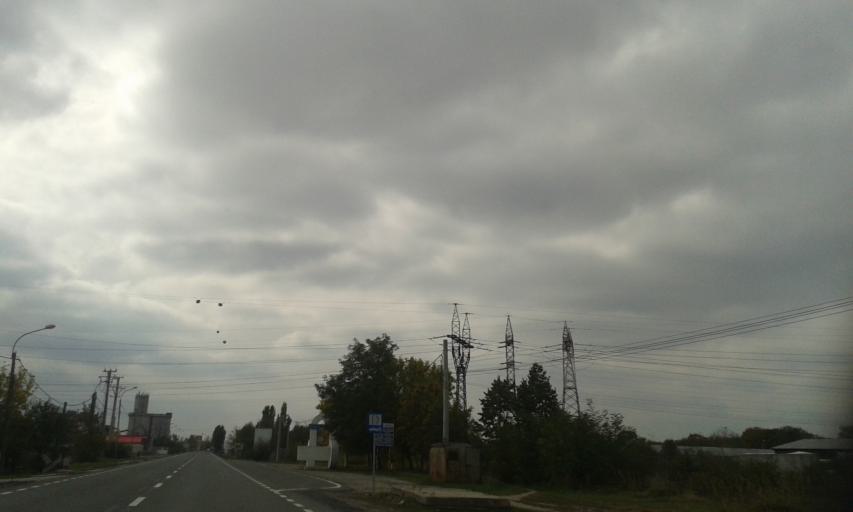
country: RO
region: Gorj
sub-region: Comuna Turcinesti
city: Turcinesti
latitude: 45.0812
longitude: 23.3144
